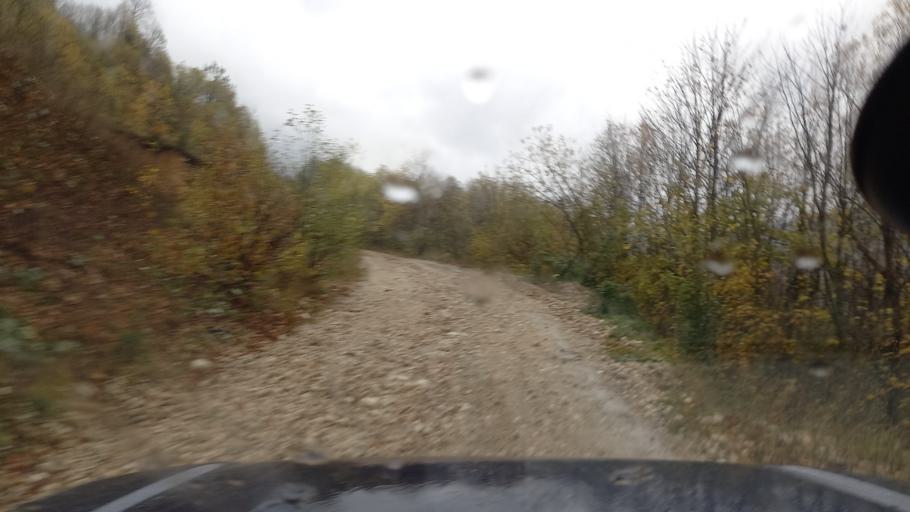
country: RU
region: Krasnodarskiy
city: Neftegorsk
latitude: 44.0234
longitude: 39.8384
